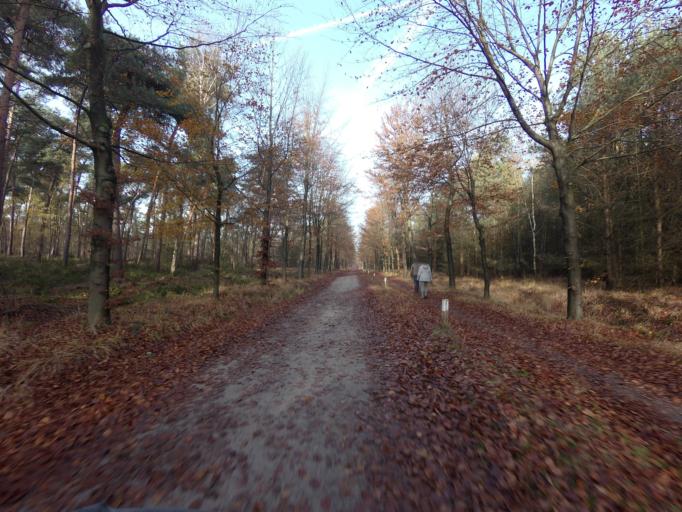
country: NL
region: North Brabant
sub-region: Gemeente Breda
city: Breda
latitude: 51.5528
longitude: 4.7692
